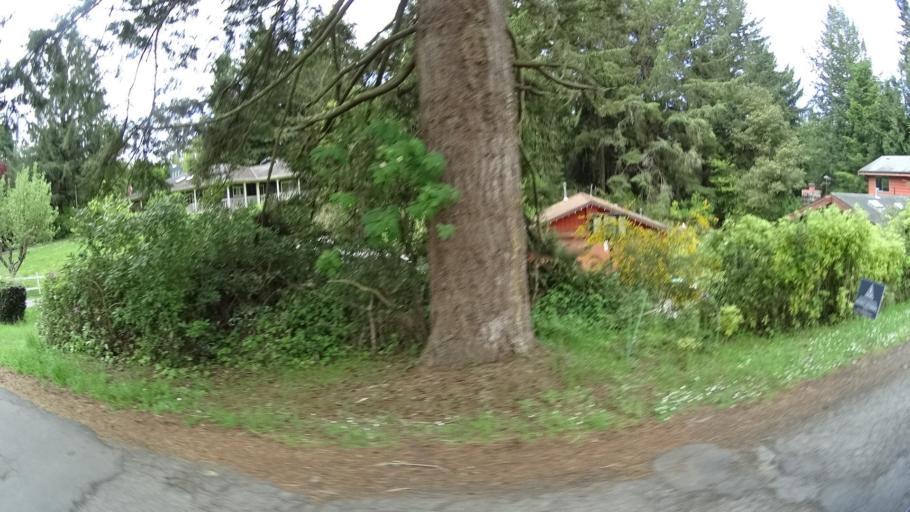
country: US
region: California
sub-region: Humboldt County
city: Bayside
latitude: 40.8473
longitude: -124.0540
